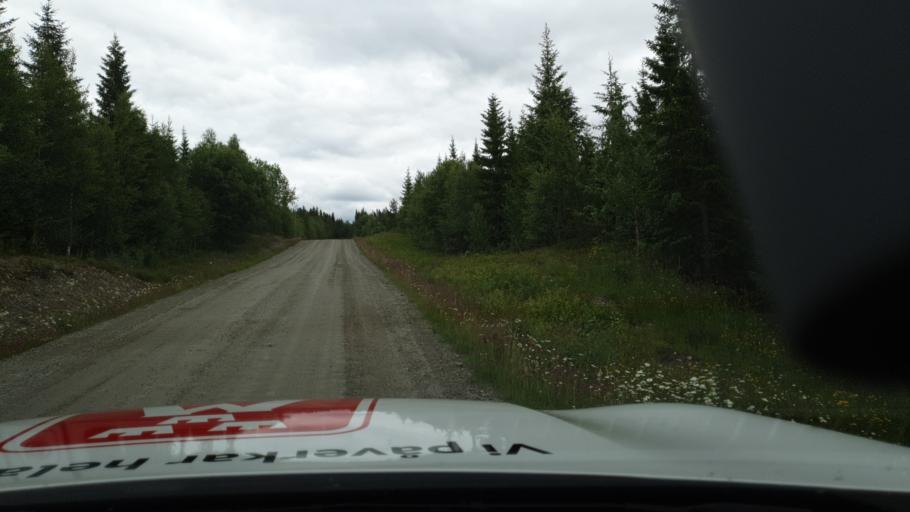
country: SE
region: Vaesterbotten
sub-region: Storumans Kommun
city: Storuman
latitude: 64.7883
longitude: 17.0175
